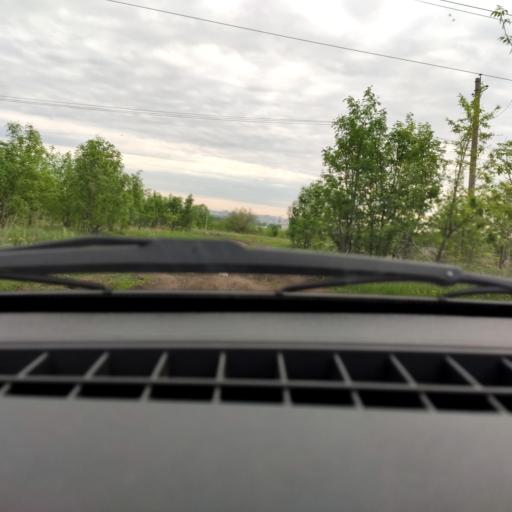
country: RU
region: Bashkortostan
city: Avdon
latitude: 54.6985
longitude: 55.8065
